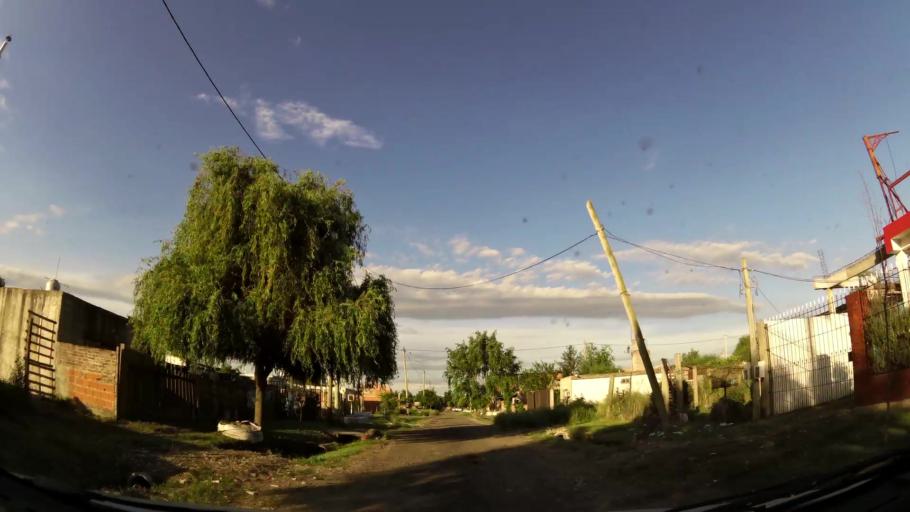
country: AR
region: Buenos Aires
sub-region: Partido de Merlo
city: Merlo
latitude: -34.7005
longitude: -58.7536
